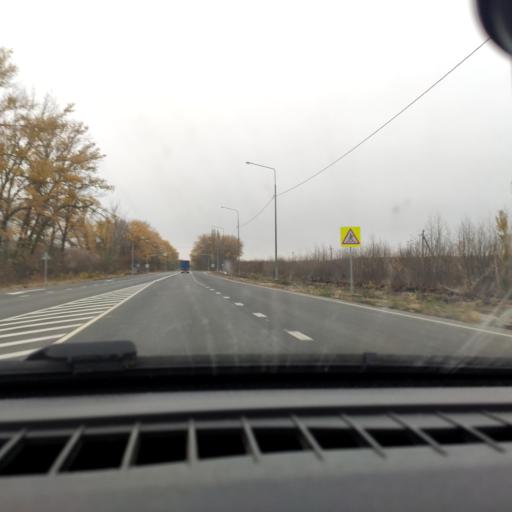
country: RU
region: Voronezj
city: Uryv-Pokrovka
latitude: 51.1720
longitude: 39.0759
